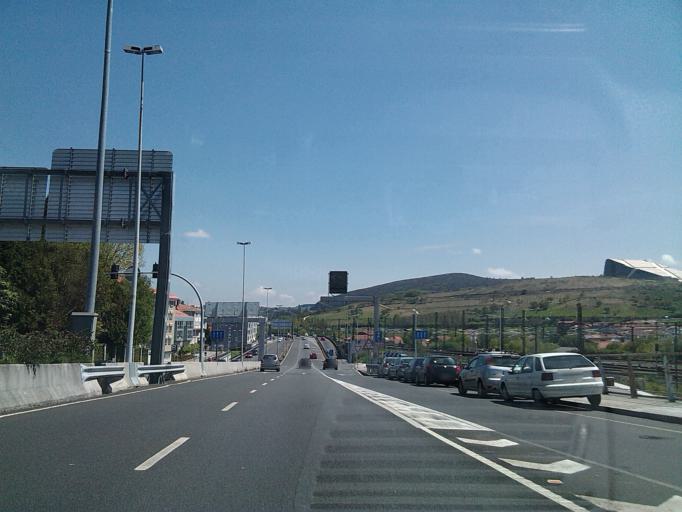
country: ES
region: Galicia
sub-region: Provincia da Coruna
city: Santiago de Compostela
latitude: 42.8724
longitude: -8.5418
